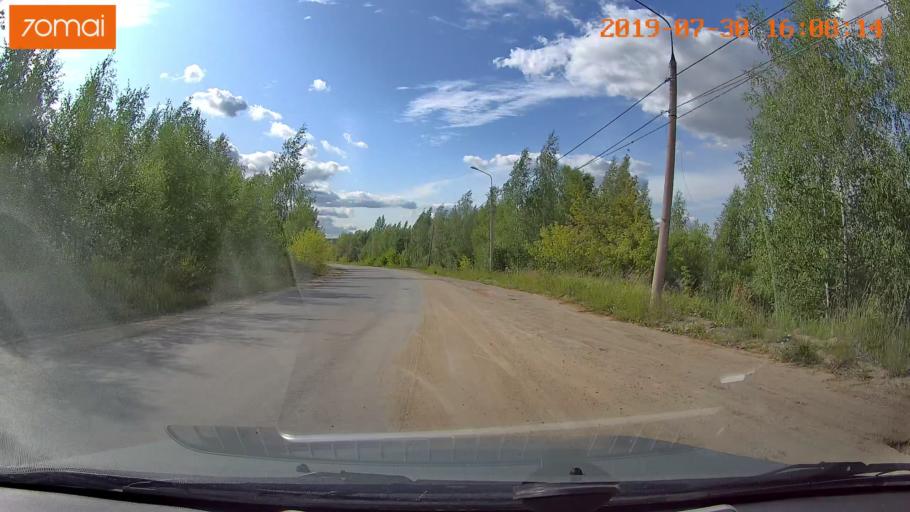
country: RU
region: Moskovskaya
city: Peski
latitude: 55.2477
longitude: 38.7252
